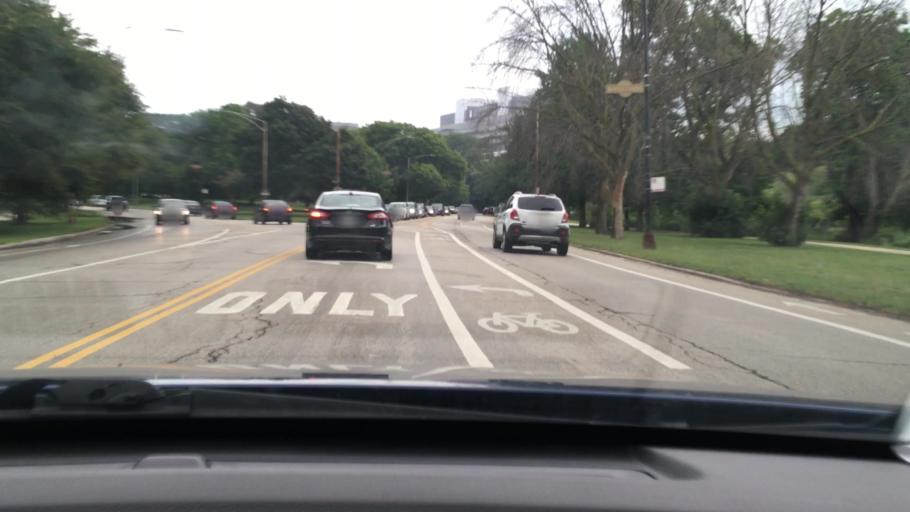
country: US
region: Illinois
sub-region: Cook County
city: Chicago
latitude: 41.7933
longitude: -87.6115
